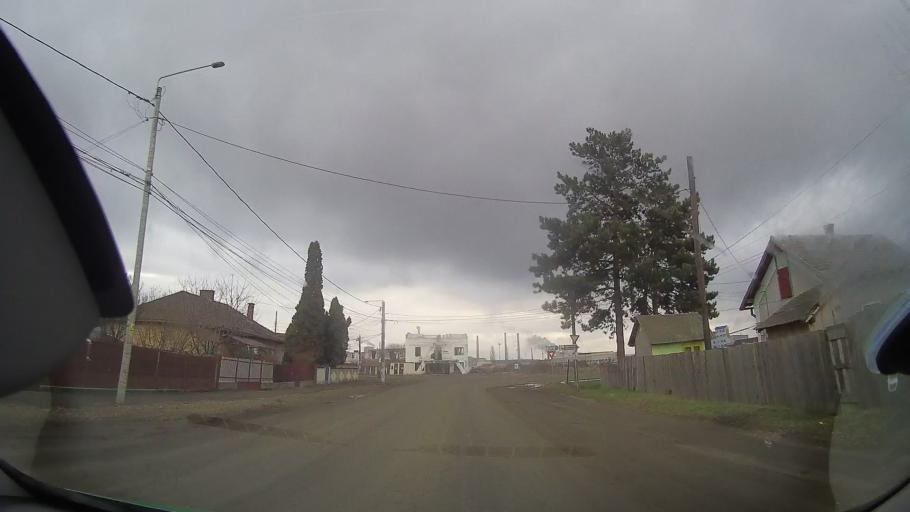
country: RO
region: Cluj
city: Turda
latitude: 46.5486
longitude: 23.7834
